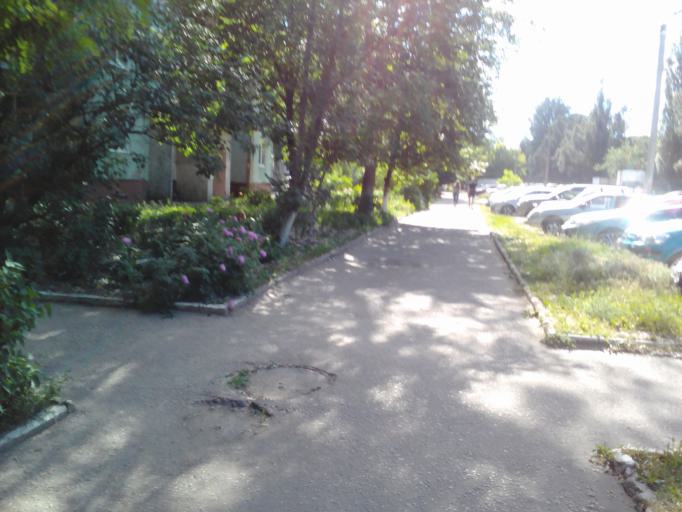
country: RU
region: Kursk
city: Voroshnevo
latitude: 51.6675
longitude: 36.0900
